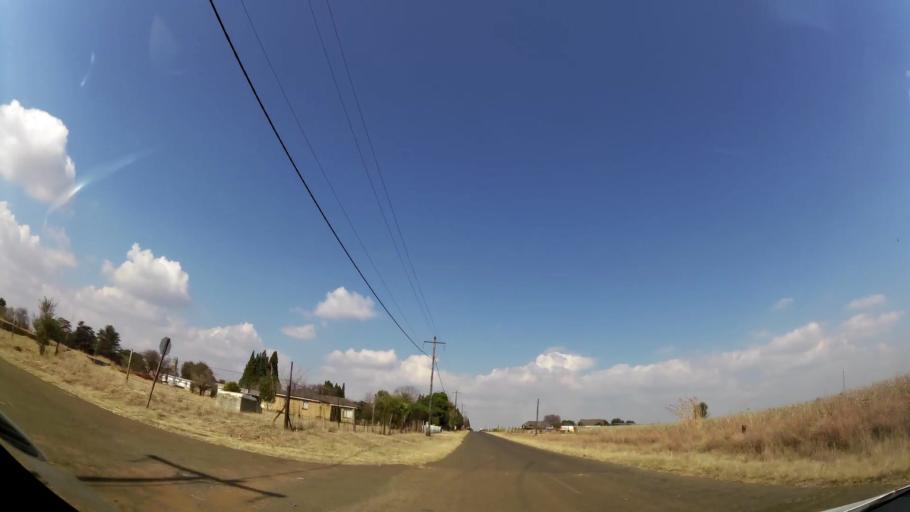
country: ZA
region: Gauteng
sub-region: Ekurhuleni Metropolitan Municipality
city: Springs
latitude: -26.1846
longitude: 28.5335
